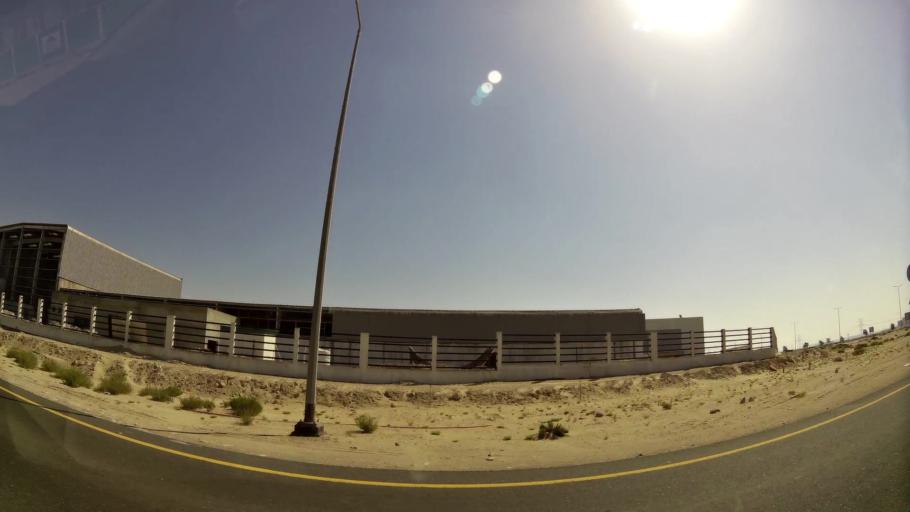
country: AE
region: Dubai
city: Dubai
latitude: 24.9122
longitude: 55.0715
